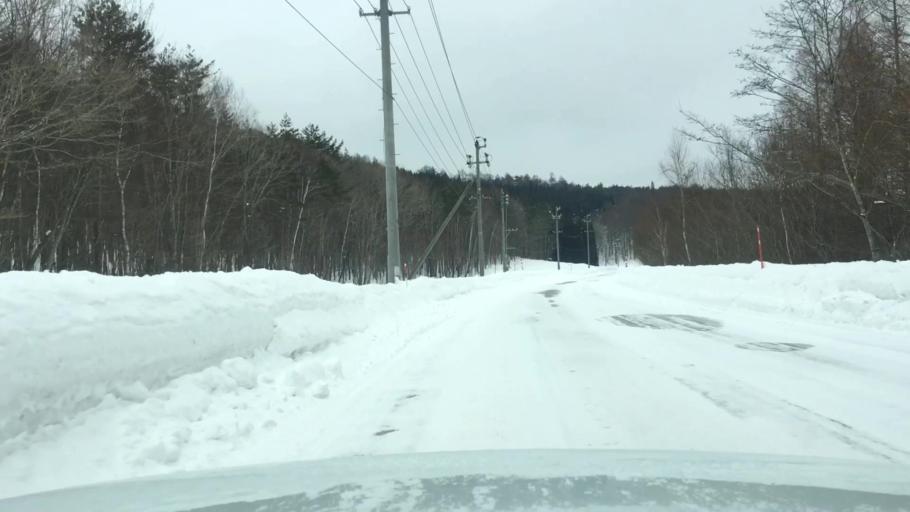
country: JP
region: Iwate
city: Shizukuishi
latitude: 39.9760
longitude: 141.0008
